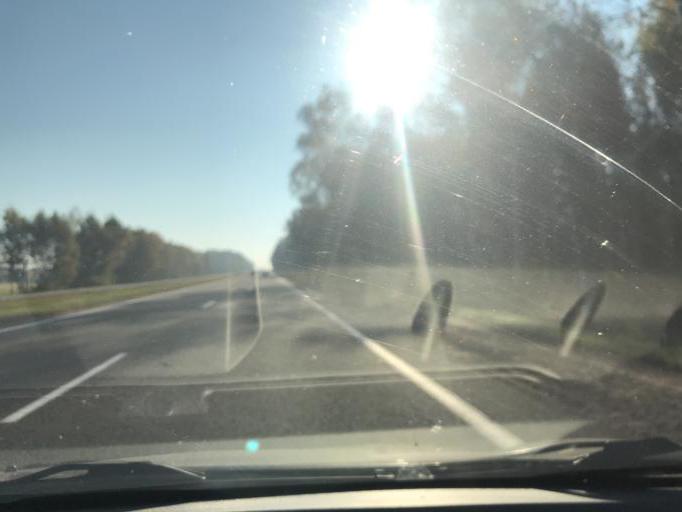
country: BY
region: Minsk
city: Dukora
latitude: 53.6273
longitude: 28.0306
